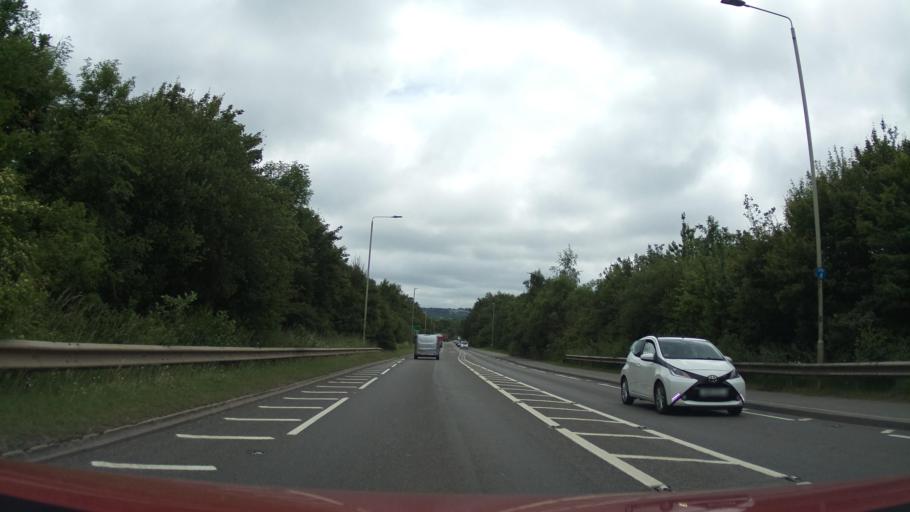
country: GB
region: England
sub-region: Leicestershire
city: Coalville
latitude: 52.7327
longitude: -1.3809
